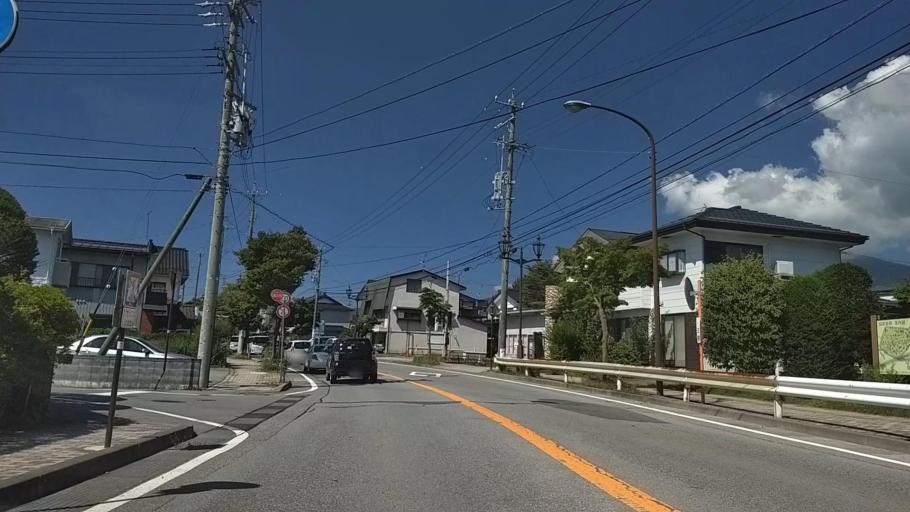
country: JP
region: Nagano
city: Komoro
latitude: 36.3488
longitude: 138.5949
